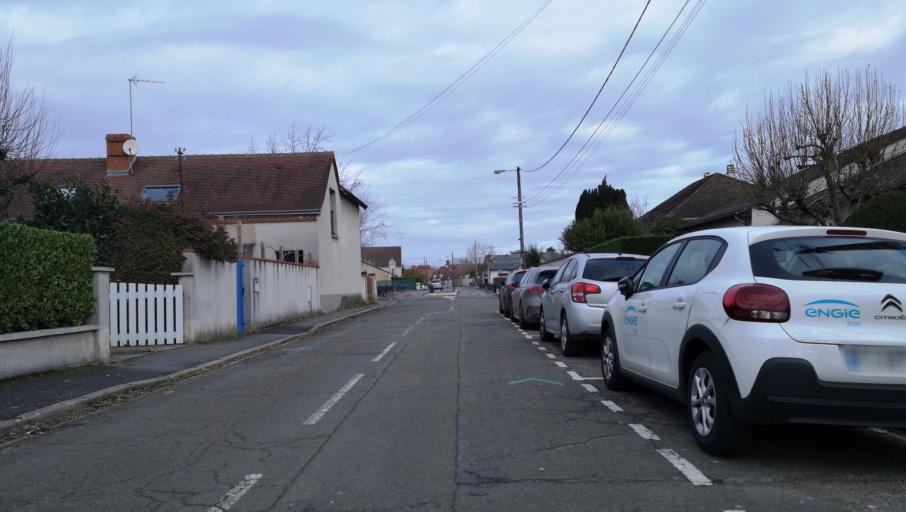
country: FR
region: Centre
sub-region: Departement du Loiret
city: Saint-Jean-de-Braye
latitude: 47.9116
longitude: 1.9617
